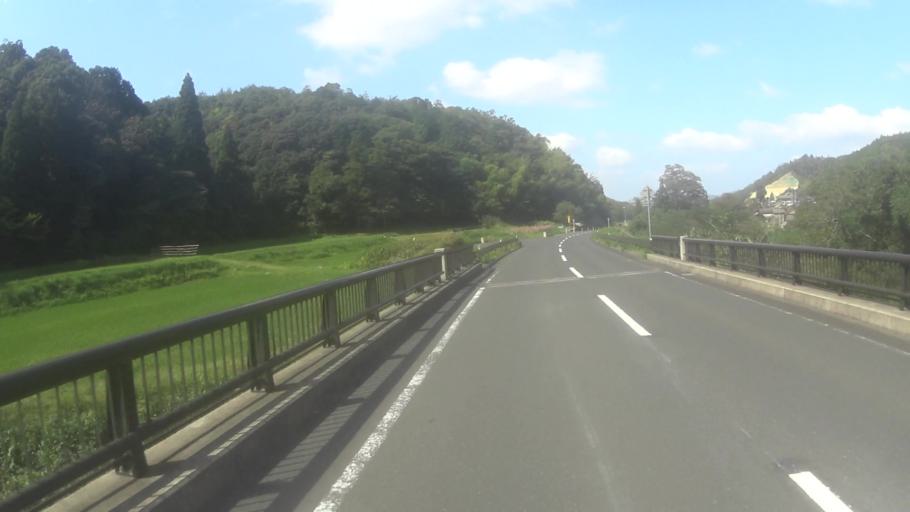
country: JP
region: Kyoto
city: Miyazu
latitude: 35.6466
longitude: 135.1276
